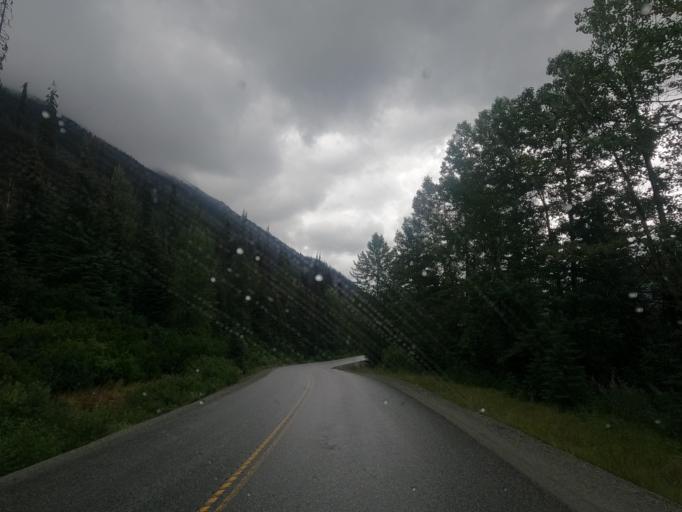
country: CA
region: British Columbia
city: Pemberton
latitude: 50.3849
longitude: -122.4399
